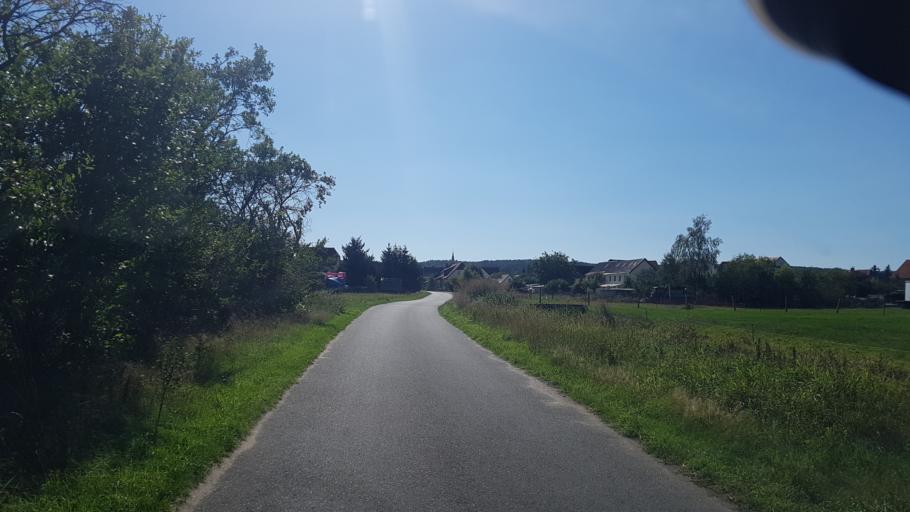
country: DE
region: Brandenburg
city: Hirschfeld
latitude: 51.3938
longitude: 13.6250
